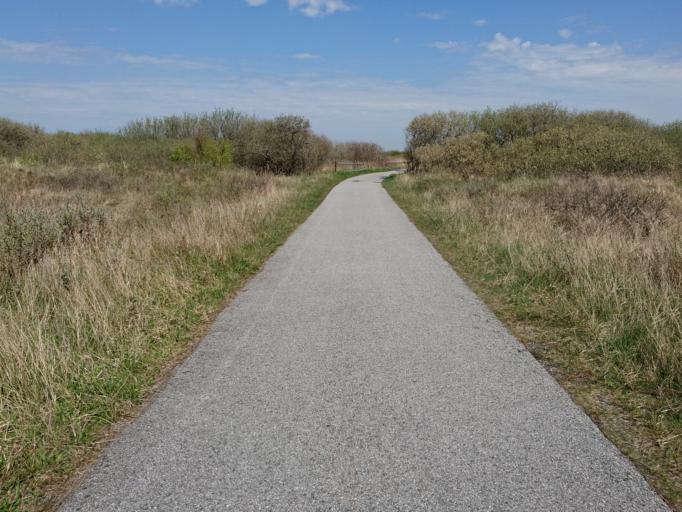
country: DK
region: North Denmark
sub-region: Frederikshavn Kommune
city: Skagen
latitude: 57.6747
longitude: 10.4980
